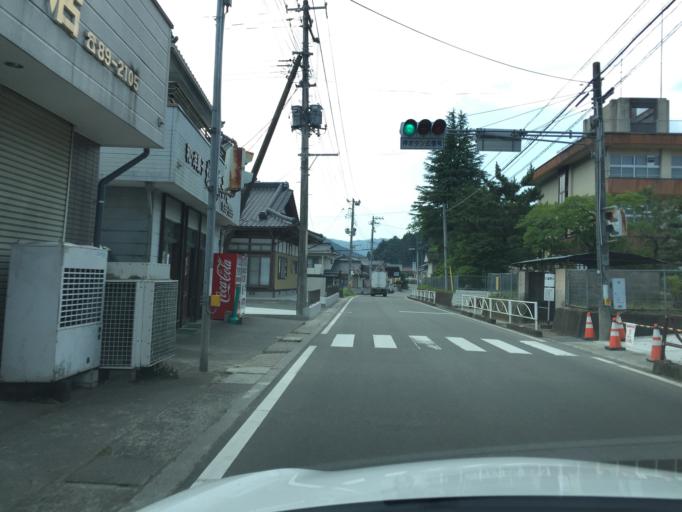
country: JP
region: Fukushima
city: Iwaki
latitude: 37.0362
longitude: 140.7076
